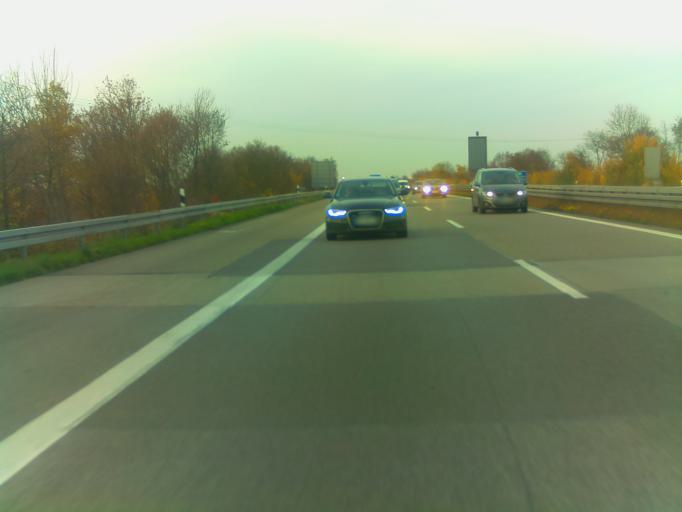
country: DE
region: Baden-Wuerttemberg
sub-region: Karlsruhe Region
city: Heddesheim
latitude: 49.5157
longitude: 8.6384
